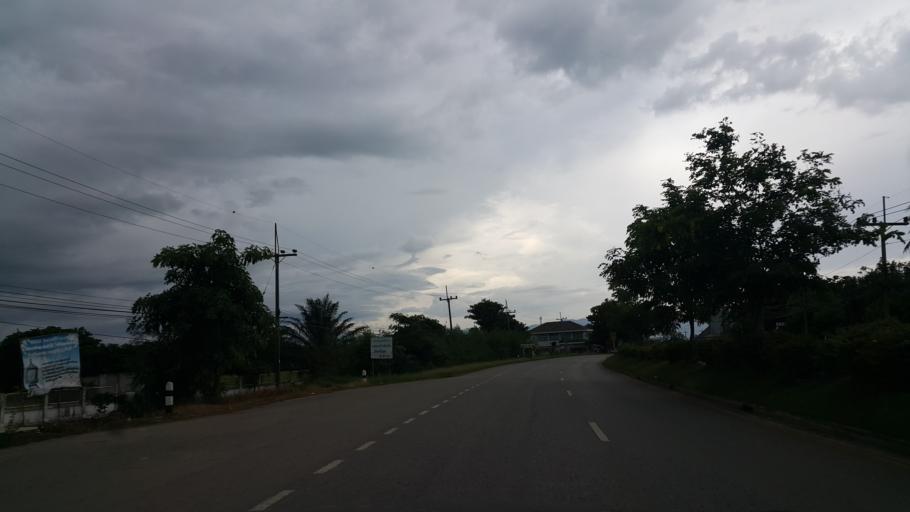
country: TH
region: Phayao
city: Dok Kham Tai
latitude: 19.1549
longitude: 99.9414
